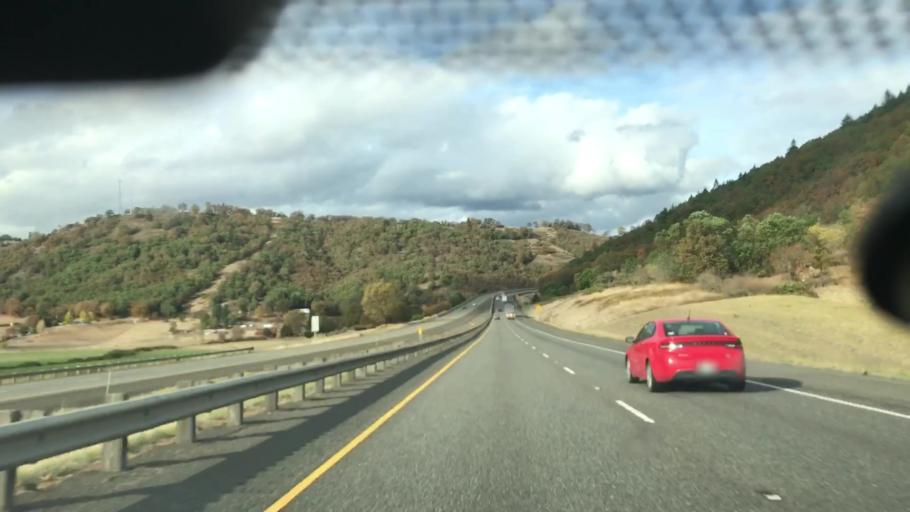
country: US
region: Oregon
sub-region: Douglas County
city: Winston
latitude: 43.0965
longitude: -123.3674
